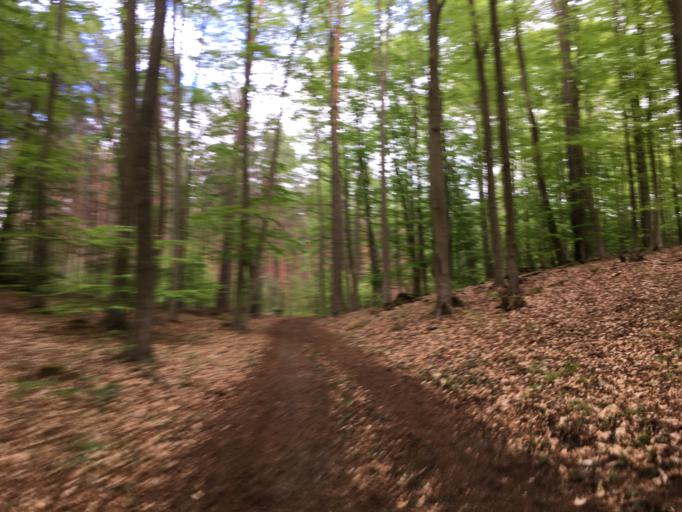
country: DE
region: Brandenburg
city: Wandlitz
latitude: 52.7598
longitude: 13.5327
